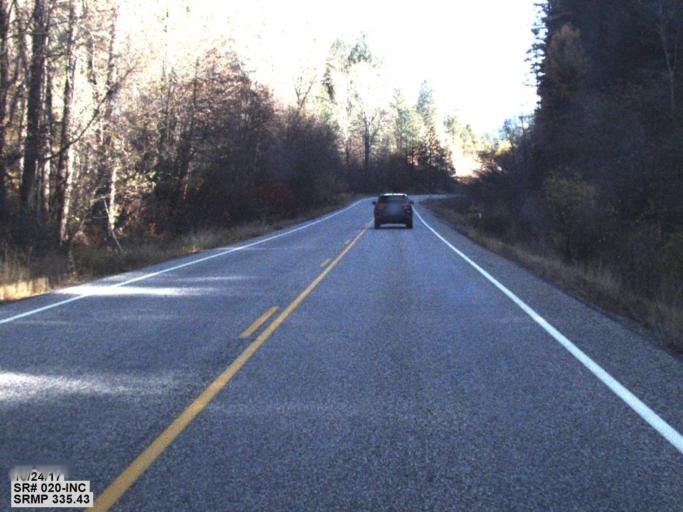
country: US
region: Washington
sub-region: Stevens County
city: Kettle Falls
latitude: 48.5840
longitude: -118.2192
